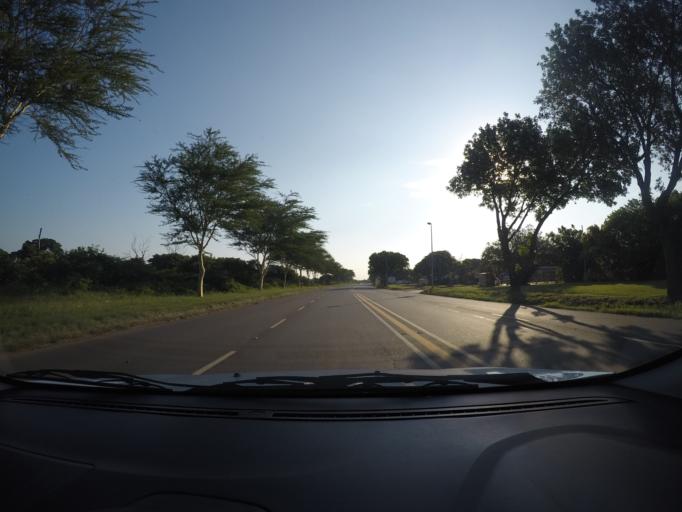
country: ZA
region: KwaZulu-Natal
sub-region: uThungulu District Municipality
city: Richards Bay
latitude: -28.7645
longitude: 32.0197
